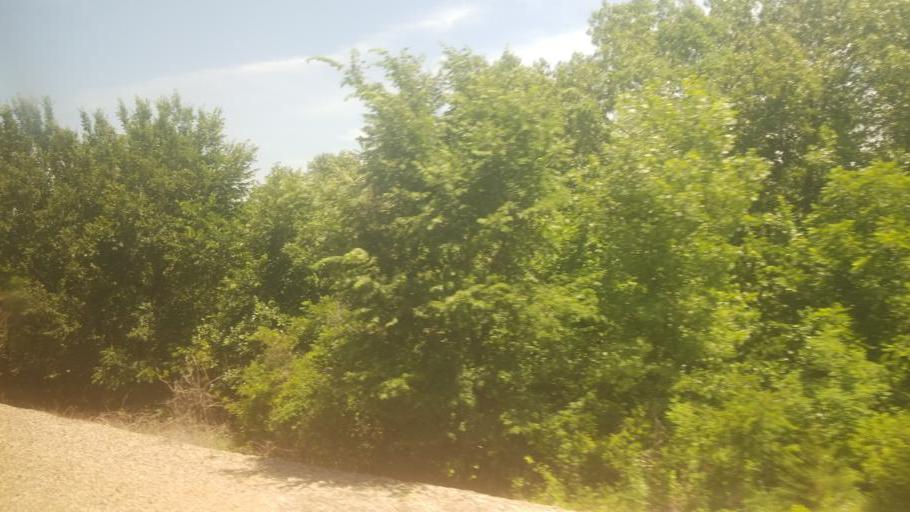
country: US
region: Missouri
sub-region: Linn County
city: Marceline
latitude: 39.8380
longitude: -92.8229
